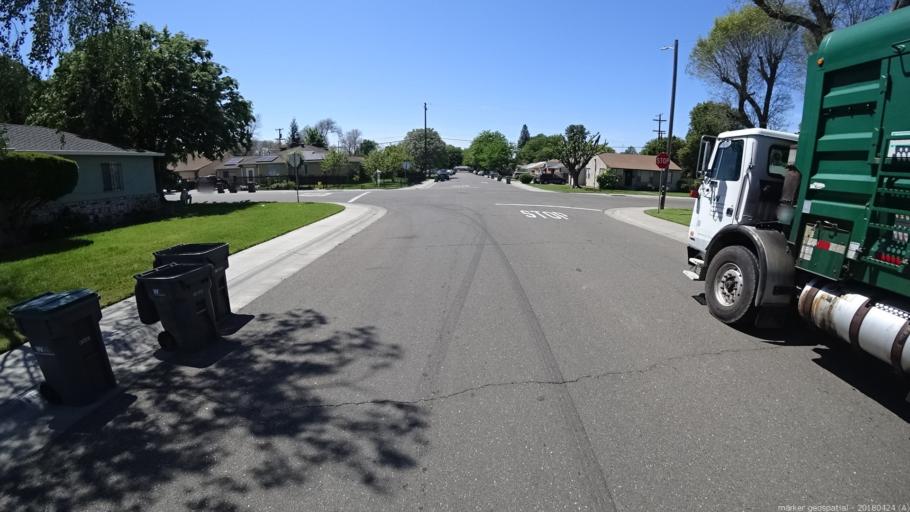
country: US
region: California
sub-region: Yolo County
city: West Sacramento
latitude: 38.5822
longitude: -121.5305
